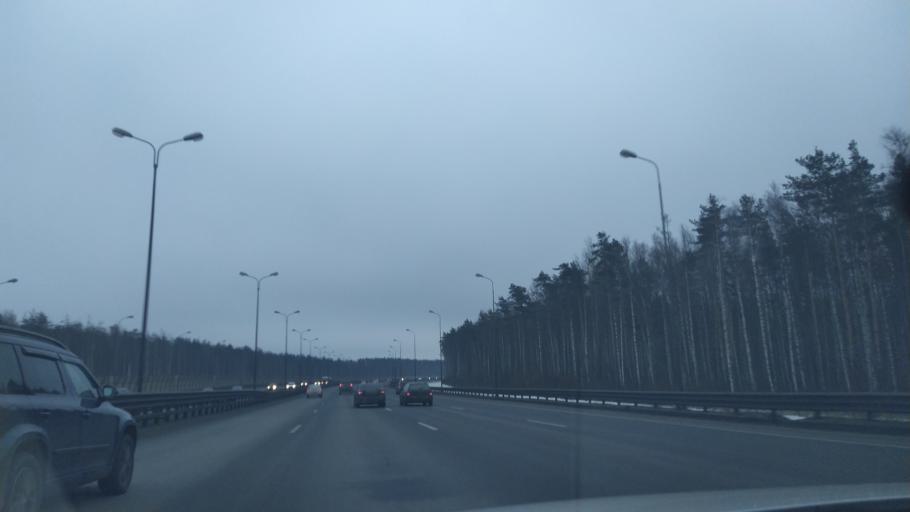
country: RU
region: St.-Petersburg
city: Krasnogvargeisky
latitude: 59.9749
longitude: 30.5387
